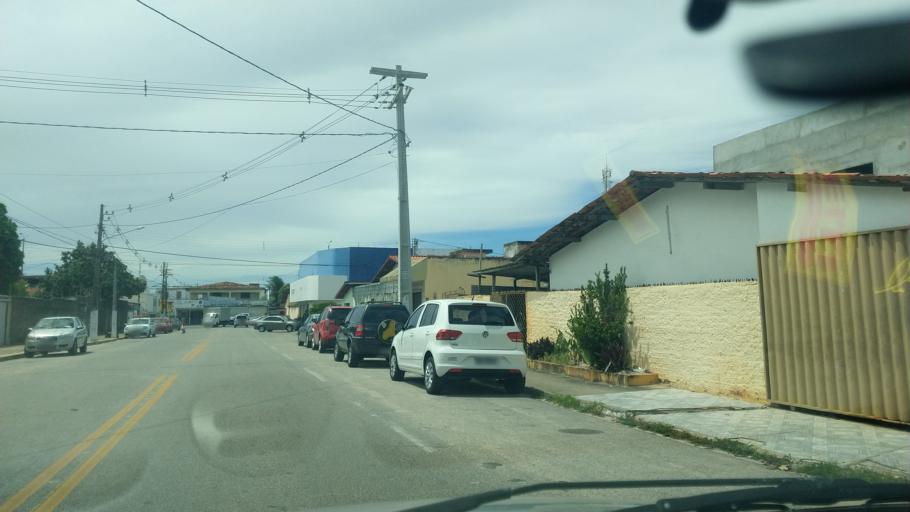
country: BR
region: Rio Grande do Norte
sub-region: Natal
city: Natal
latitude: -5.8260
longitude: -35.2356
